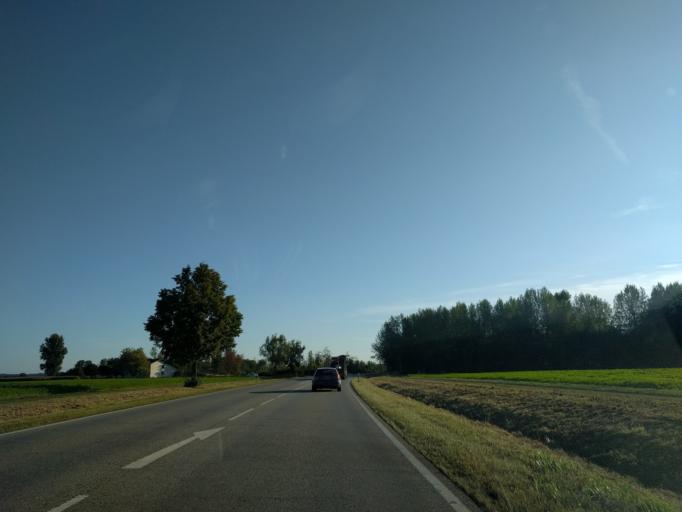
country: DE
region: Bavaria
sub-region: Lower Bavaria
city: Osterhofen
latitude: 48.6974
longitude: 13.0451
